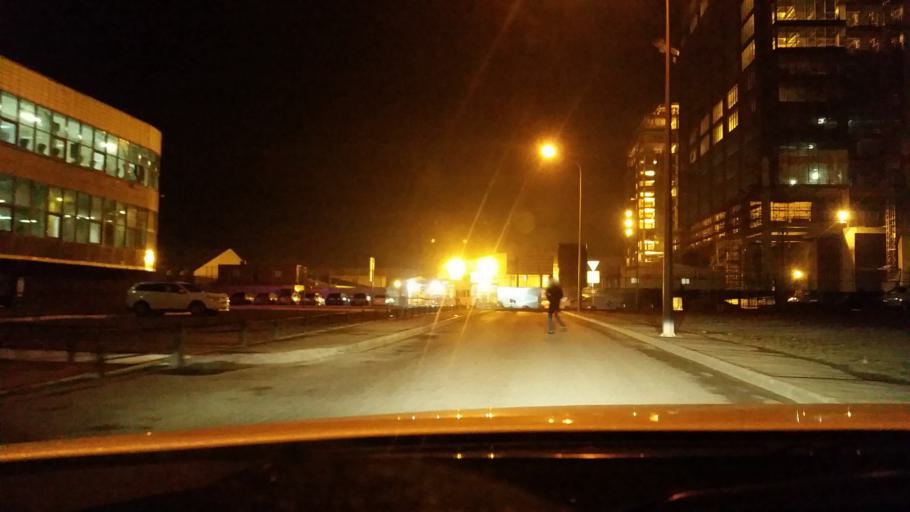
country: KZ
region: Astana Qalasy
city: Astana
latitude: 51.1204
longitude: 71.4305
